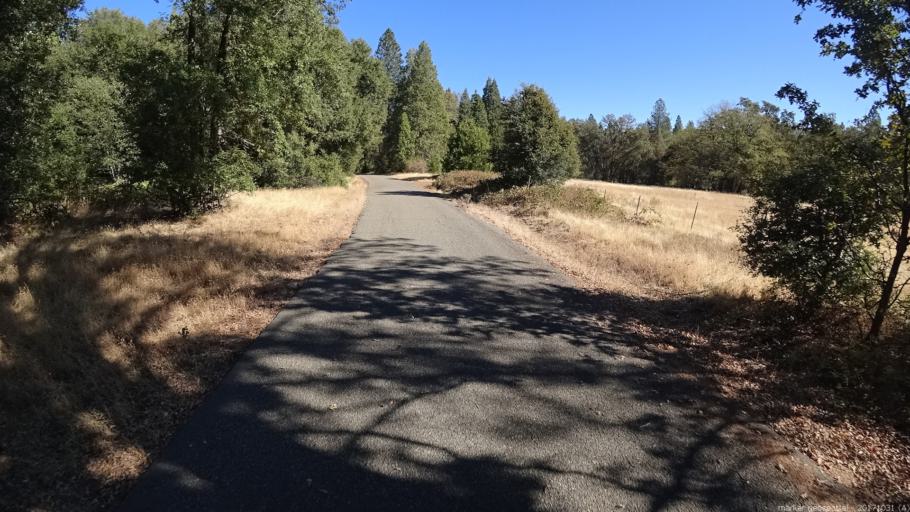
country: US
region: California
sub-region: Shasta County
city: Shingletown
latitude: 40.5334
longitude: -121.9357
